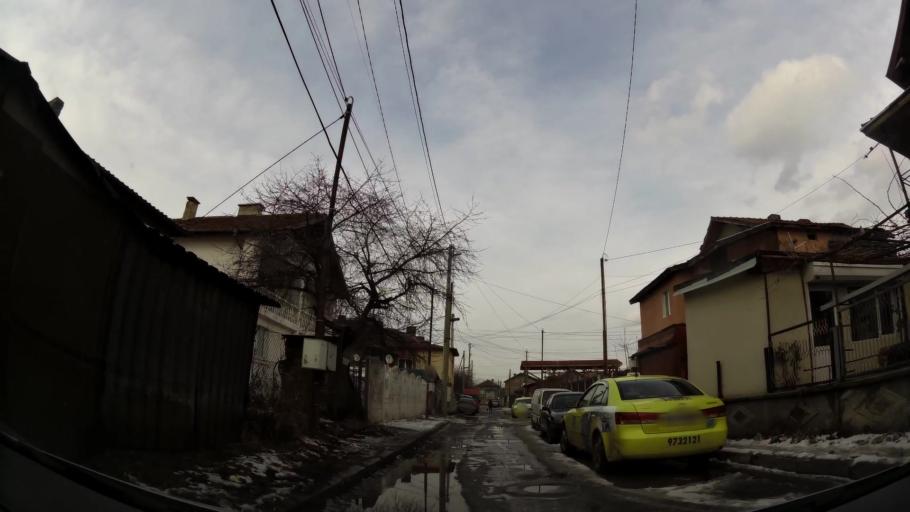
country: BG
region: Sofia-Capital
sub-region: Stolichna Obshtina
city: Sofia
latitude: 42.6872
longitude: 23.3835
